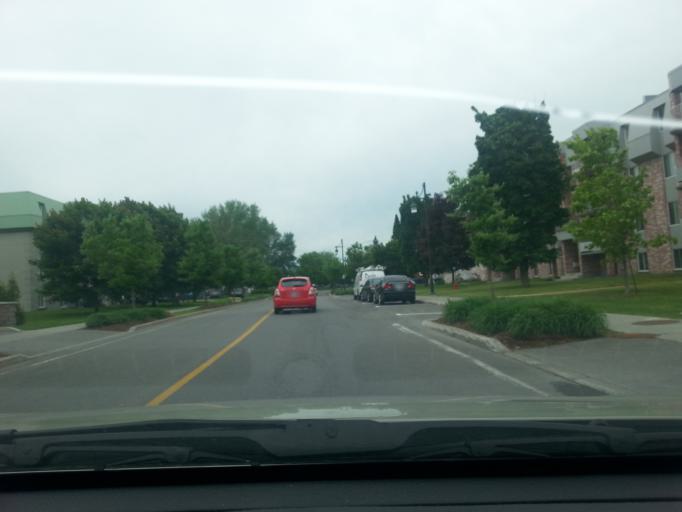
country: CA
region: Quebec
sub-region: Lanaudiere
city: Terrebonne
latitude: 45.6958
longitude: -73.6165
